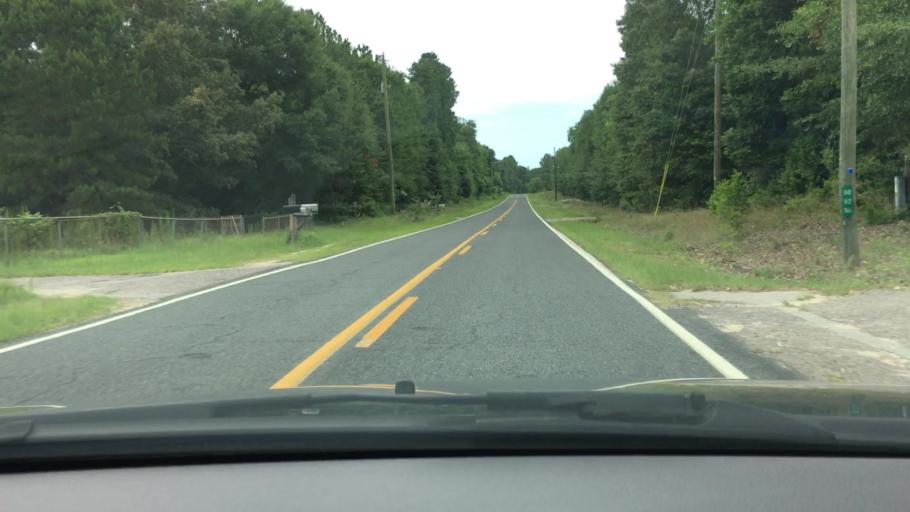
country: US
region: South Carolina
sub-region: Barnwell County
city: Williston
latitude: 33.6358
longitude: -81.3638
